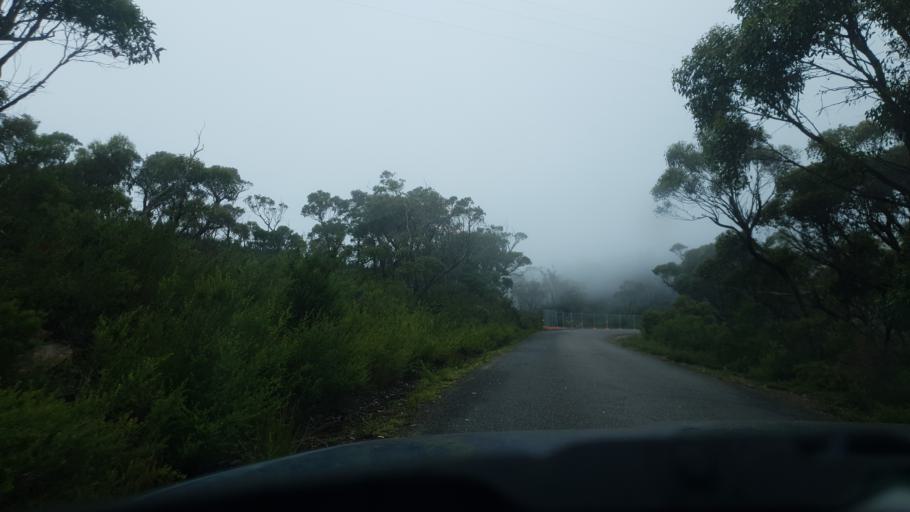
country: AU
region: Victoria
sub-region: Northern Grampians
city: Stawell
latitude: -37.2765
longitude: 142.5850
